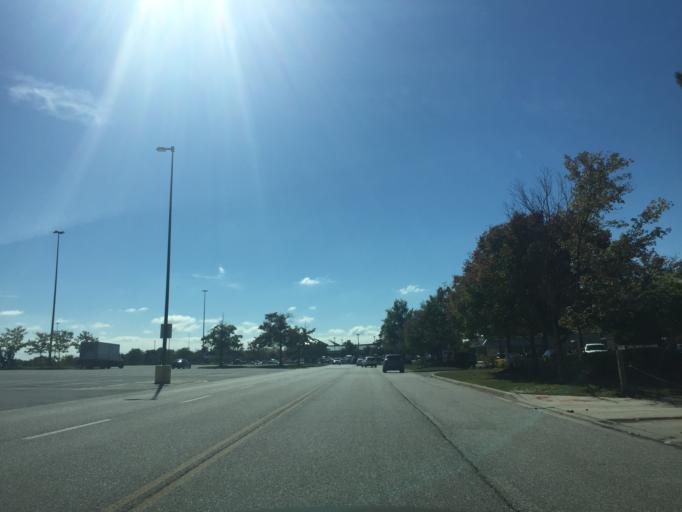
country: US
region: Maryland
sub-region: Baltimore County
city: Perry Hall
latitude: 39.3763
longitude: -76.4712
